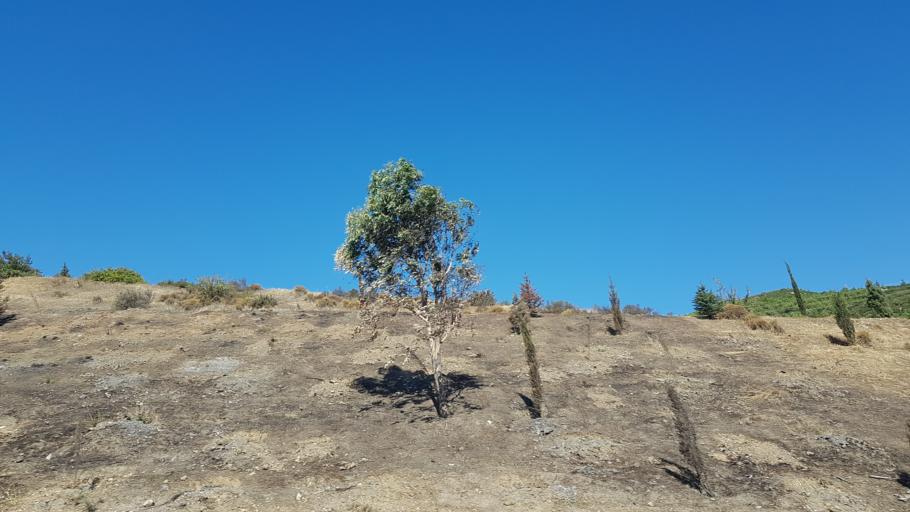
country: TR
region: Izmir
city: Buca
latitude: 38.4023
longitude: 27.2304
